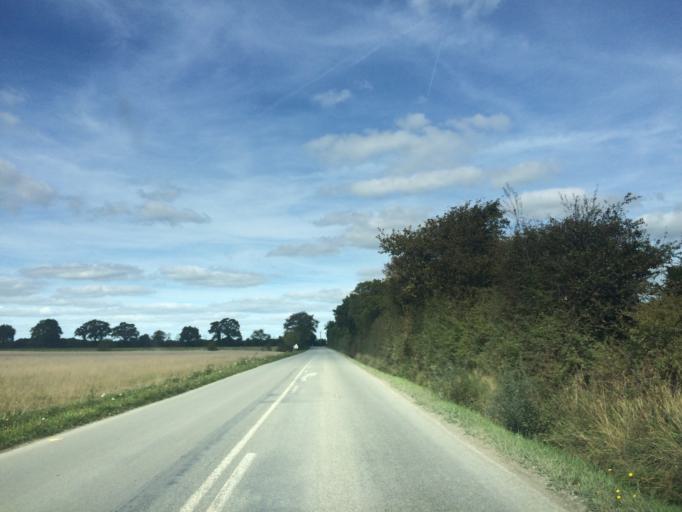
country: FR
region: Pays de la Loire
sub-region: Departement de la Loire-Atlantique
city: Rouans
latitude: 47.1606
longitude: -1.8757
